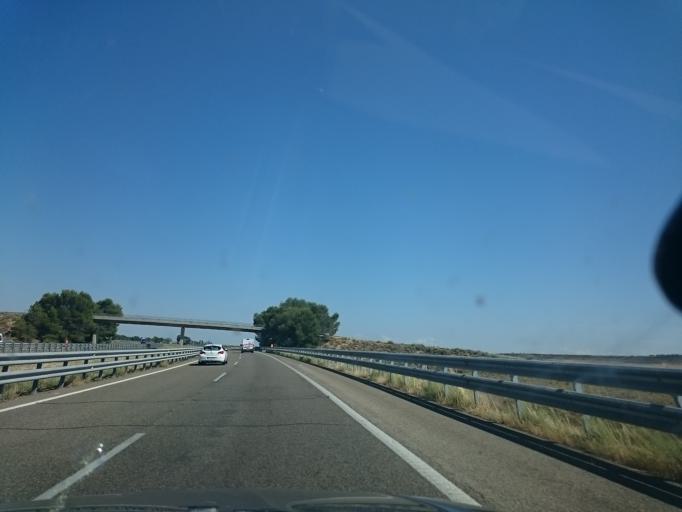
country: ES
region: Aragon
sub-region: Provincia de Huesca
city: Candasnos
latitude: 41.5114
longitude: 0.0864
